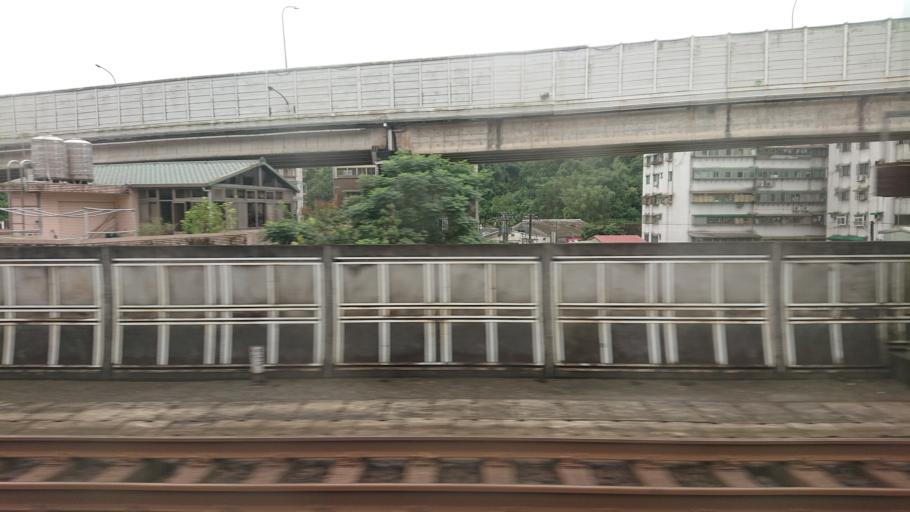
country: TW
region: Taiwan
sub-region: Keelung
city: Keelung
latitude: 25.0762
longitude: 121.6662
